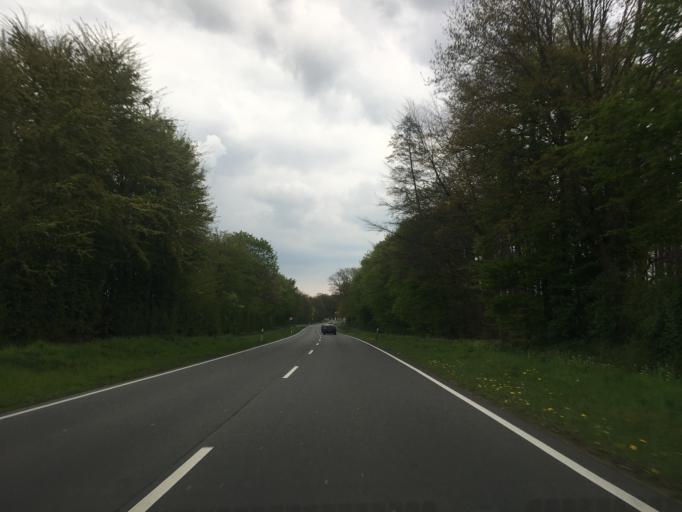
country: DE
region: North Rhine-Westphalia
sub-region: Regierungsbezirk Munster
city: Greven
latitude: 52.0944
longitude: 7.5836
